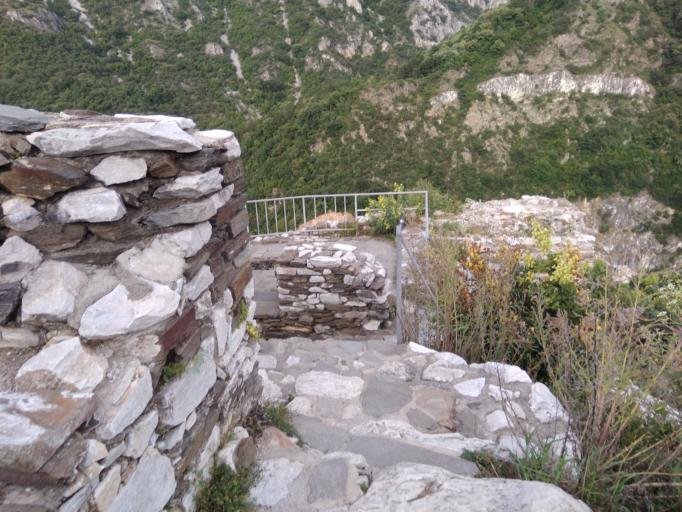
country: BG
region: Plovdiv
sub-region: Obshtina Asenovgrad
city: Asenovgrad
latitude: 41.9866
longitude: 24.8733
